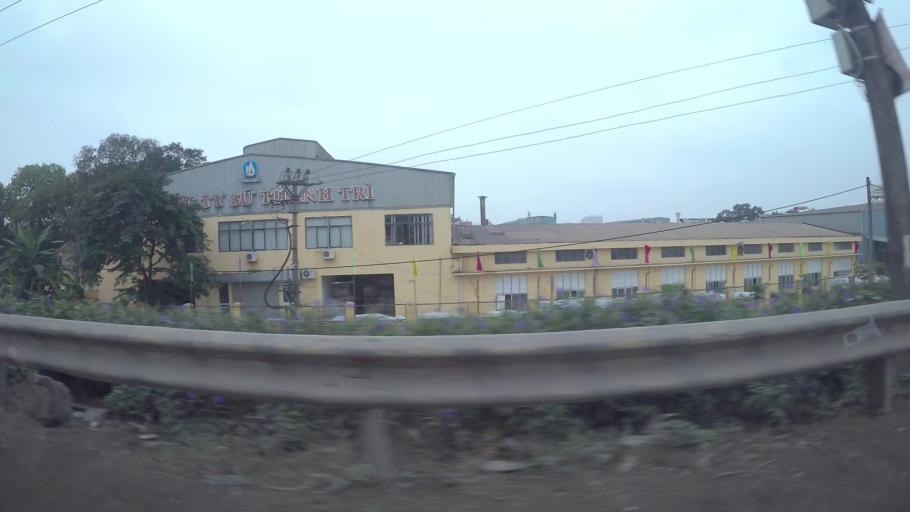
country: VN
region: Ha Noi
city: Hai BaTrung
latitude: 20.9953
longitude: 105.8925
